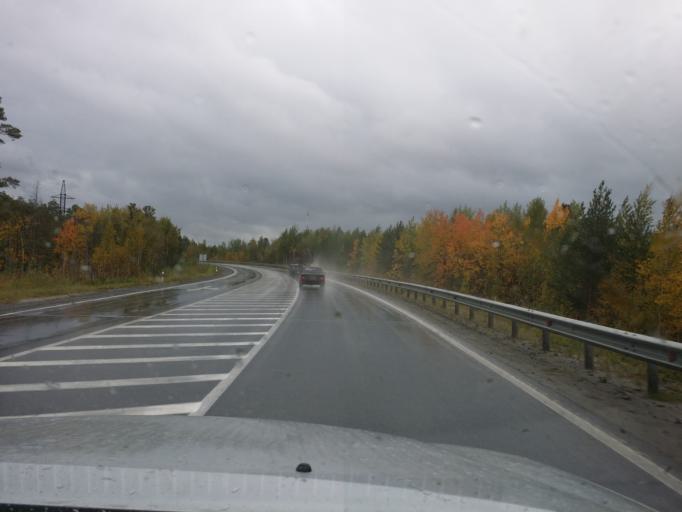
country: RU
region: Khanty-Mansiyskiy Avtonomnyy Okrug
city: Megion
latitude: 61.1332
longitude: 75.7683
